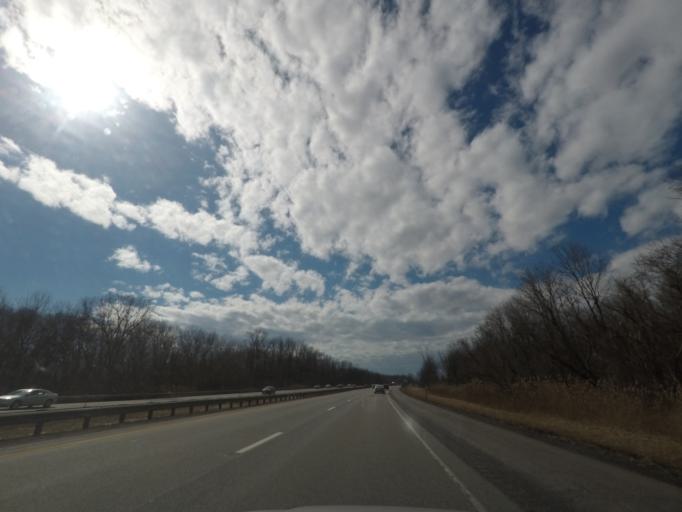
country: US
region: New York
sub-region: Madison County
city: Canastota
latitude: 43.0903
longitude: -75.7605
